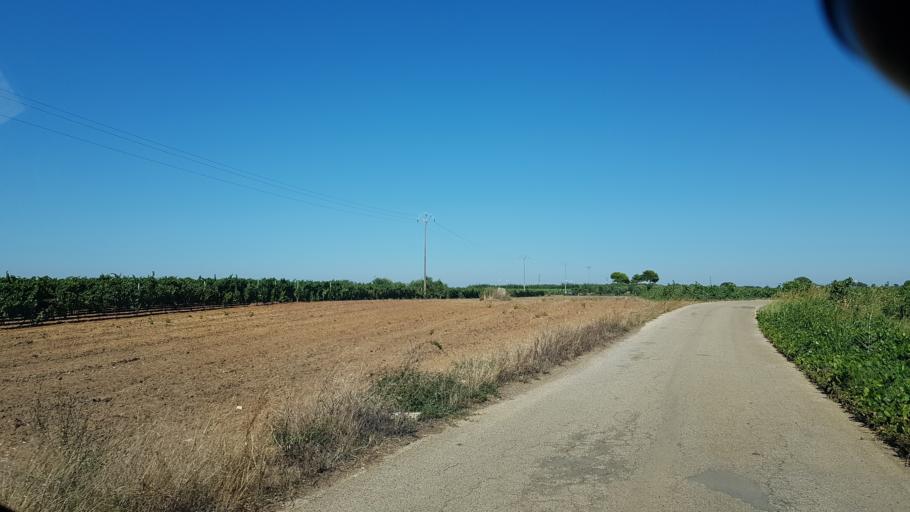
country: IT
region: Apulia
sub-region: Provincia di Brindisi
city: Tuturano
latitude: 40.5678
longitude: 17.8849
